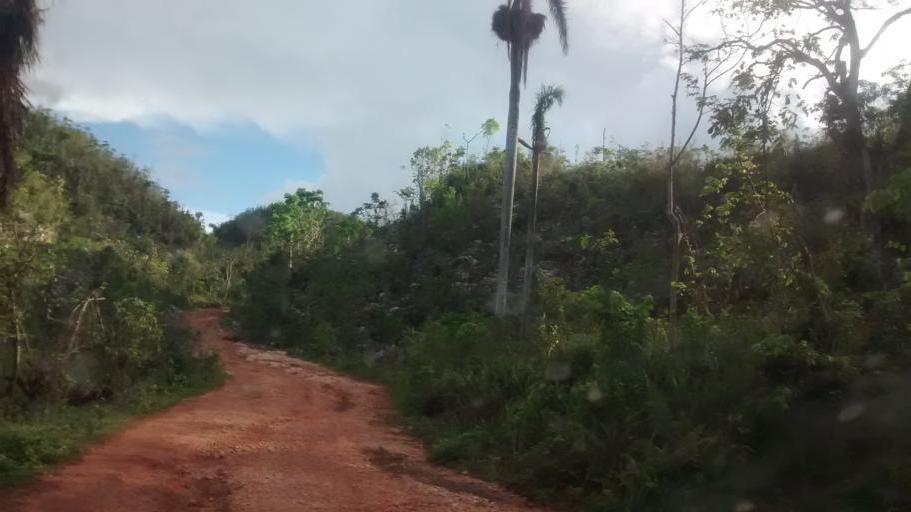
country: HT
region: Grandans
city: Corail
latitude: 18.5114
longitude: -73.7834
